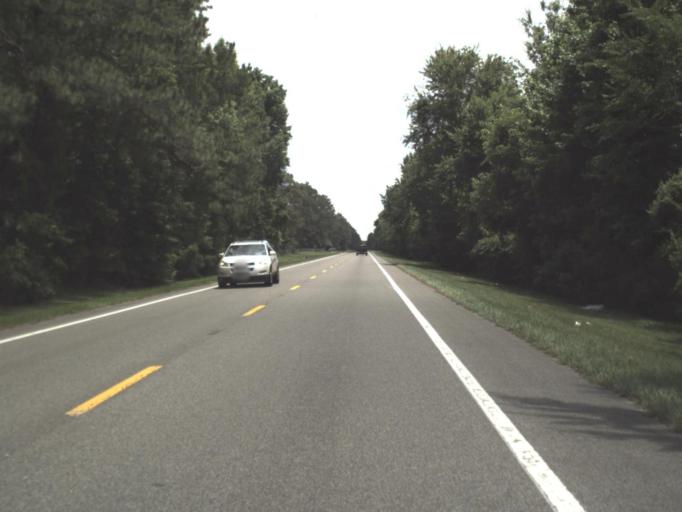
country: US
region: Florida
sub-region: Nassau County
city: Yulee
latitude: 30.6749
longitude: -81.6440
